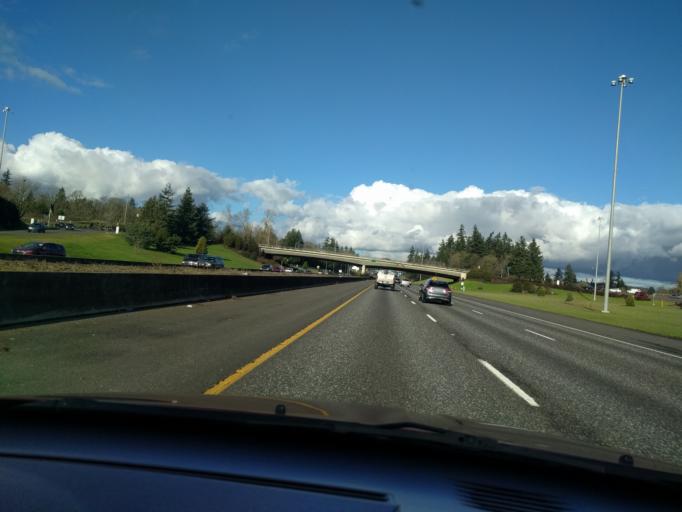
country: US
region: Oregon
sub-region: Clackamas County
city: Gladstone
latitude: 45.3827
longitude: -122.5797
